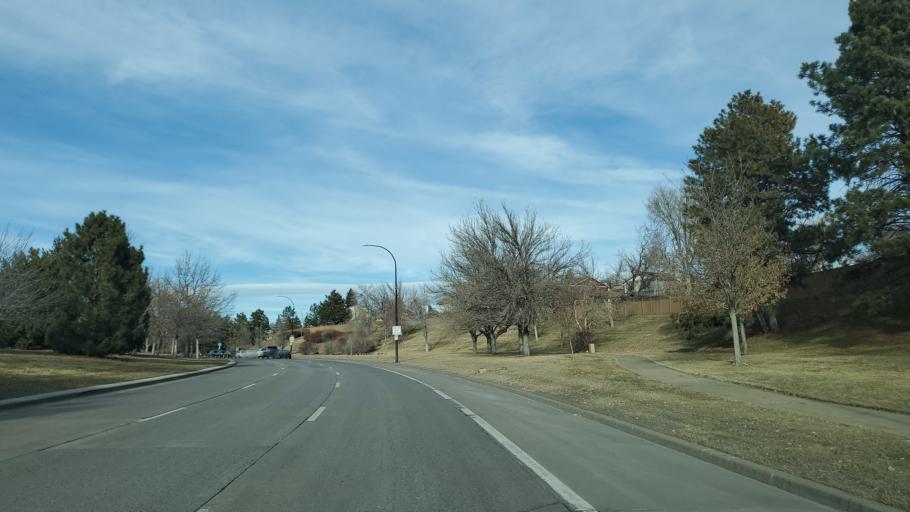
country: US
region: Colorado
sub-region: Douglas County
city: Highlands Ranch
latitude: 39.5601
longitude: -104.9864
